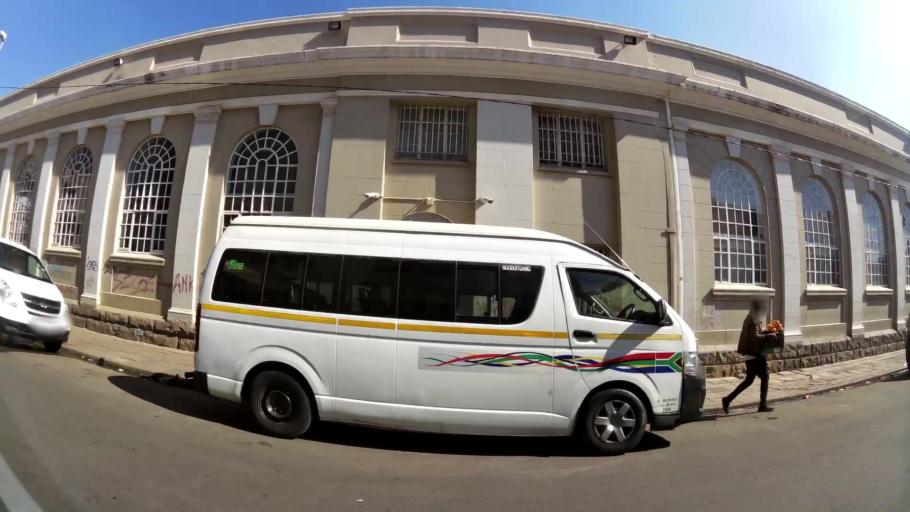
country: ZA
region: Gauteng
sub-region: City of Johannesburg Metropolitan Municipality
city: Johannesburg
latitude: -26.2015
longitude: 28.0339
